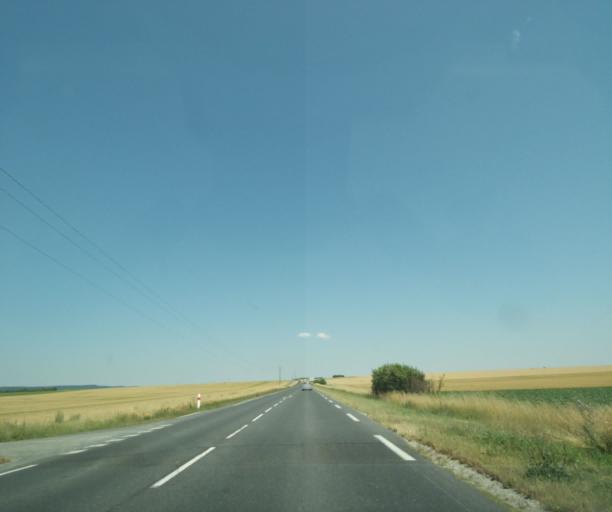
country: FR
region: Champagne-Ardenne
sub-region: Departement de la Marne
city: Mourmelon-le-Grand
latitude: 49.0935
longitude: 4.2714
